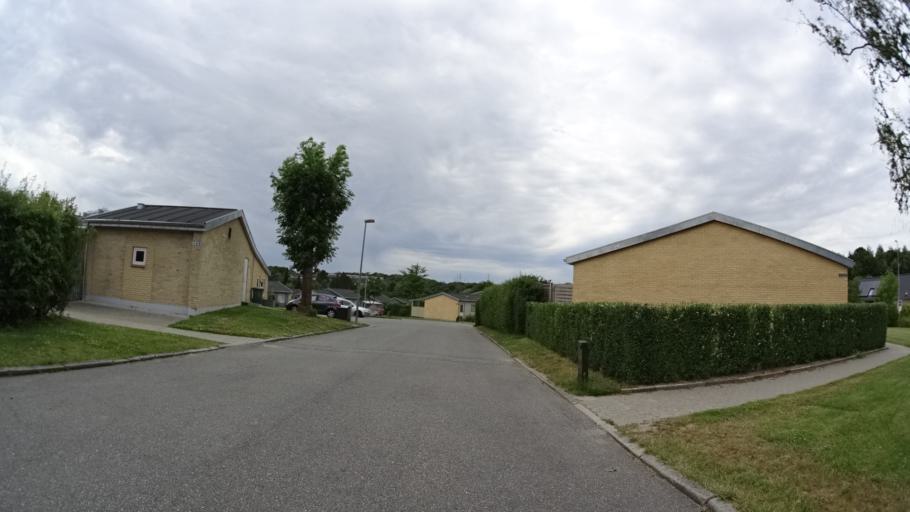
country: DK
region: Central Jutland
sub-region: Arhus Kommune
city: Stavtrup
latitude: 56.1282
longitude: 10.1435
